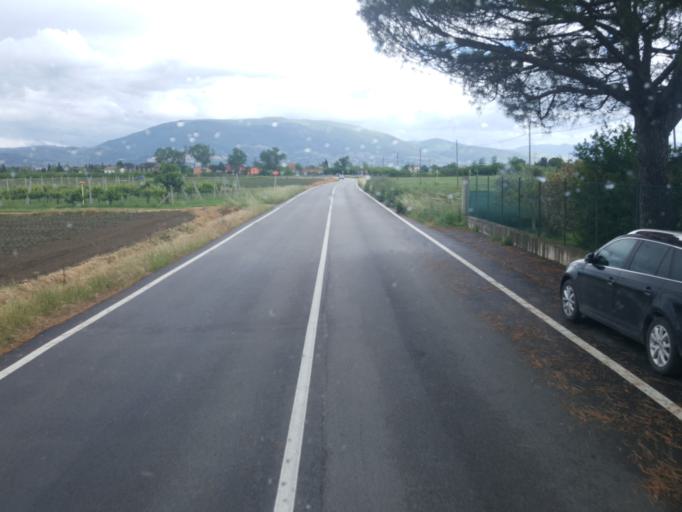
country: IT
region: Umbria
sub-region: Provincia di Perugia
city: Ospedalicchio
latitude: 43.0708
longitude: 12.5075
